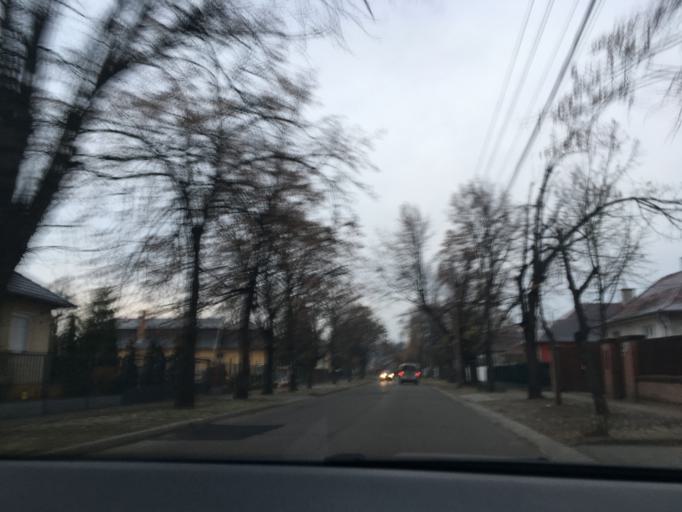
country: HU
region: Hajdu-Bihar
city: Debrecen
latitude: 47.5323
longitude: 21.6522
